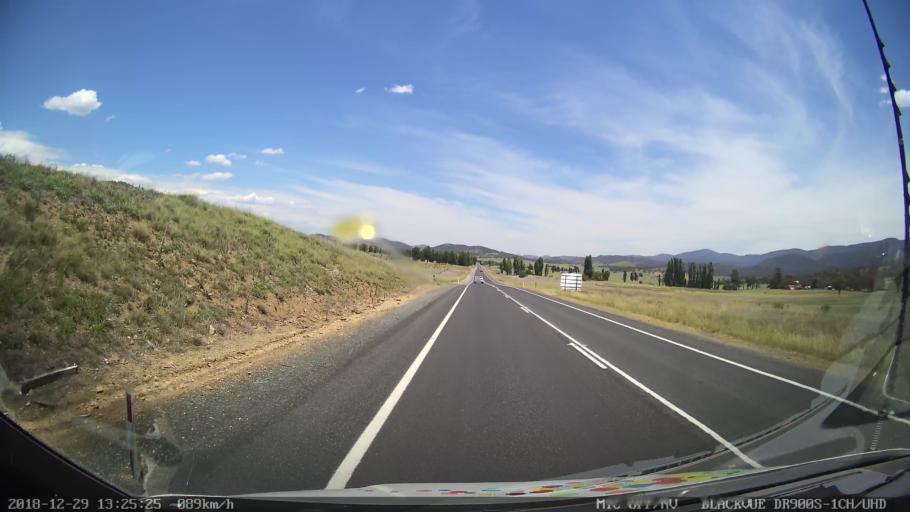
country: AU
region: New South Wales
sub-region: Cooma-Monaro
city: Cooma
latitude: -35.8421
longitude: 149.1614
